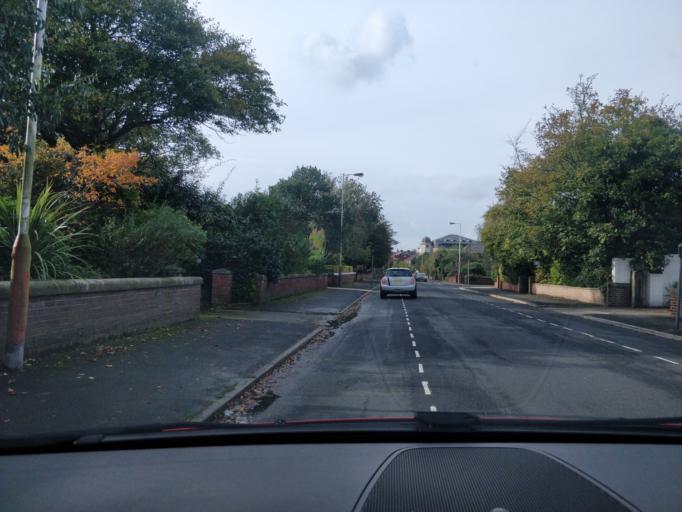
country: GB
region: England
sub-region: Sefton
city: Southport
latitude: 53.6307
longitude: -3.0222
